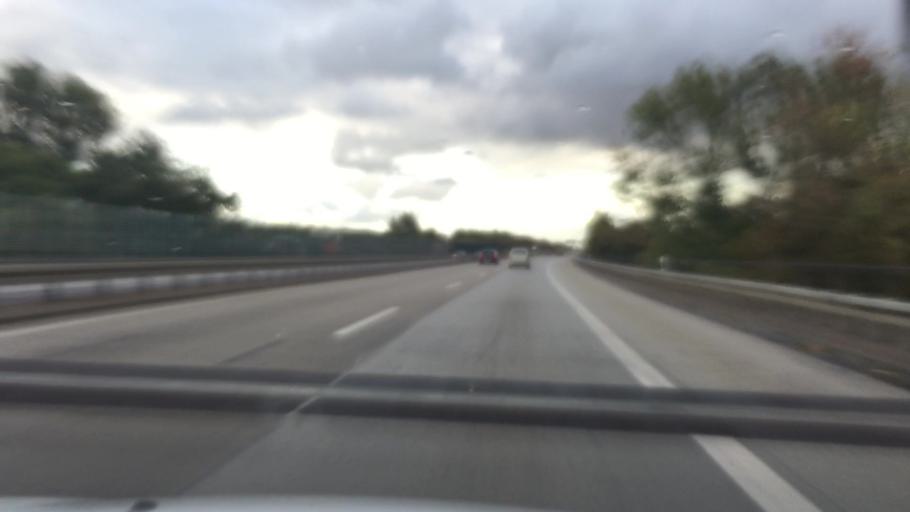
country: DE
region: Saxony-Anhalt
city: Welsleben
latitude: 52.0451
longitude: 11.6293
